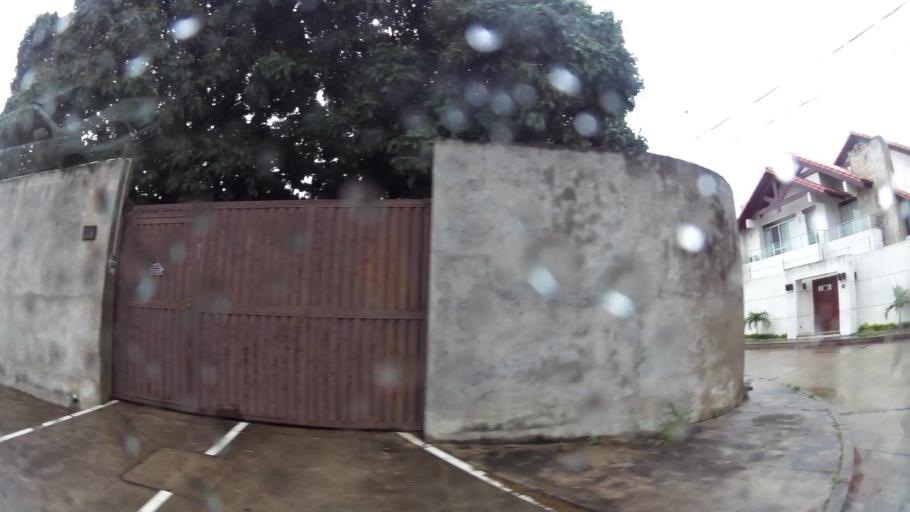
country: BO
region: Santa Cruz
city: Santa Cruz de la Sierra
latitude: -17.8048
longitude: -63.1595
